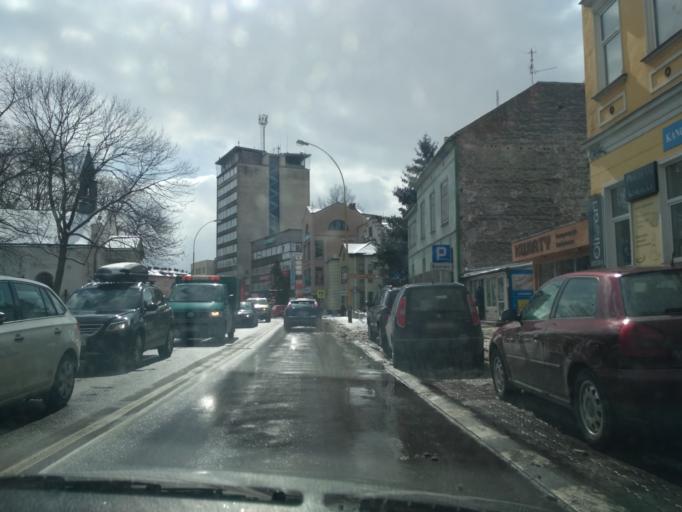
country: PL
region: Subcarpathian Voivodeship
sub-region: Rzeszow
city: Rzeszow
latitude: 50.0381
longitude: 22.0098
